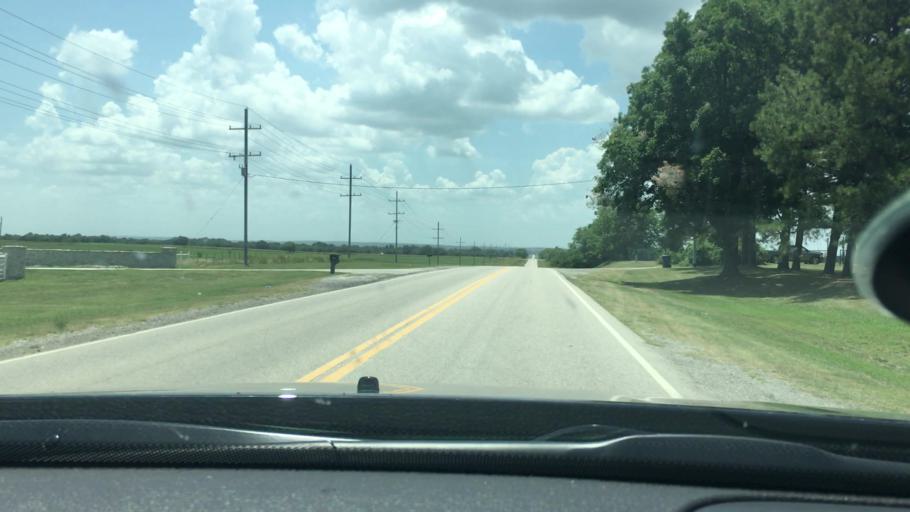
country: US
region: Oklahoma
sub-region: Pontotoc County
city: Ada
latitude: 34.6729
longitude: -96.6349
